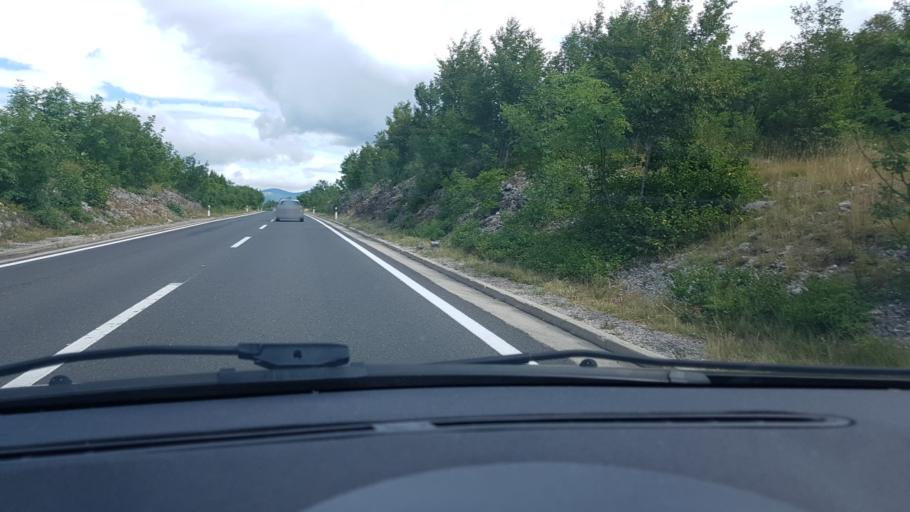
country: HR
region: Zadarska
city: Gracac
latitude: 44.4594
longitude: 15.8135
